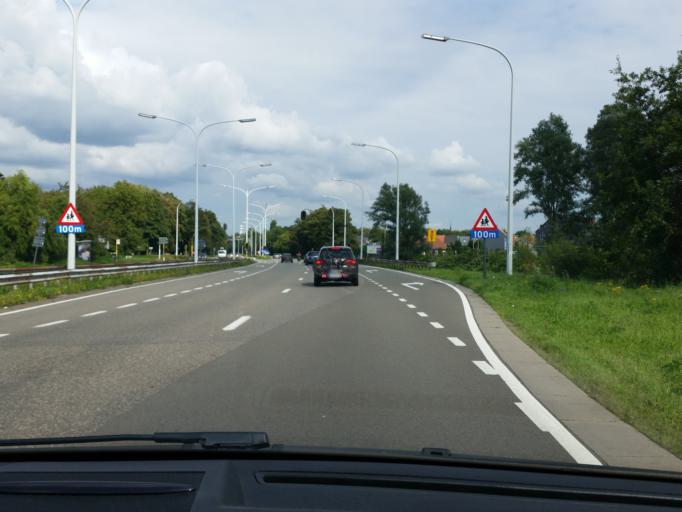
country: BE
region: Flanders
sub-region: Provincie Antwerpen
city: Kontich
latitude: 51.1289
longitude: 4.4350
